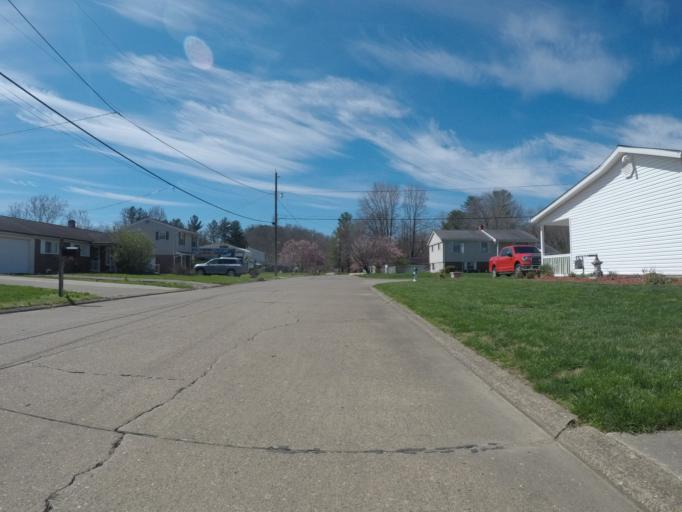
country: US
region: West Virginia
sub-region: Cabell County
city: Pea Ridge
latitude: 38.3985
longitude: -82.3166
